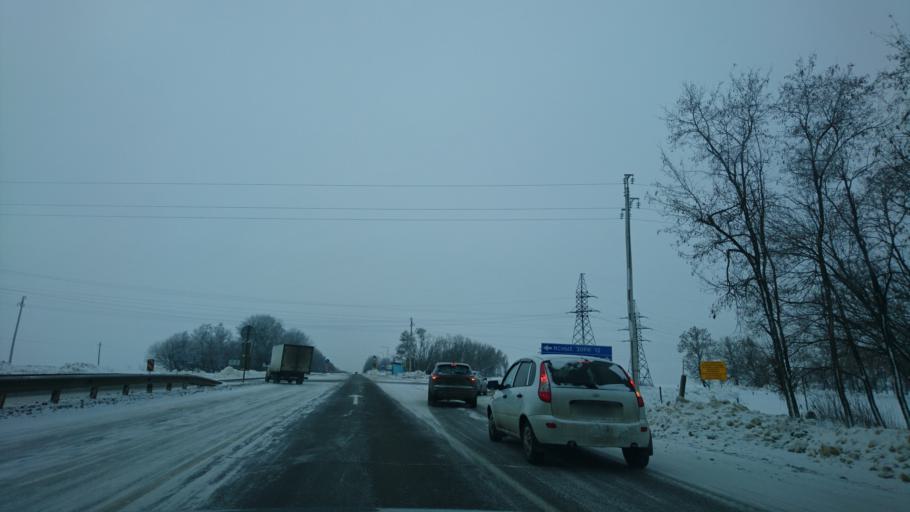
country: RU
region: Belgorod
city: Mayskiy
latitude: 50.4375
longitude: 36.3911
